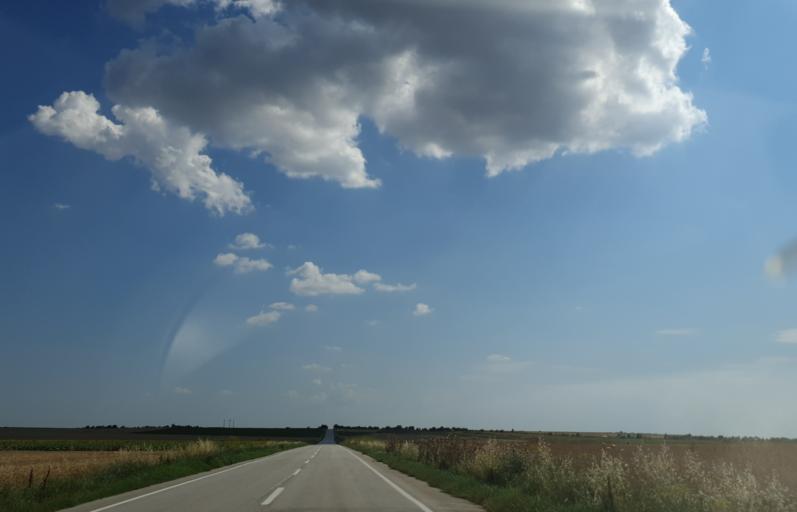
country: TR
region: Kirklareli
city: Buyukkaristiran
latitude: 41.3918
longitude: 27.5720
